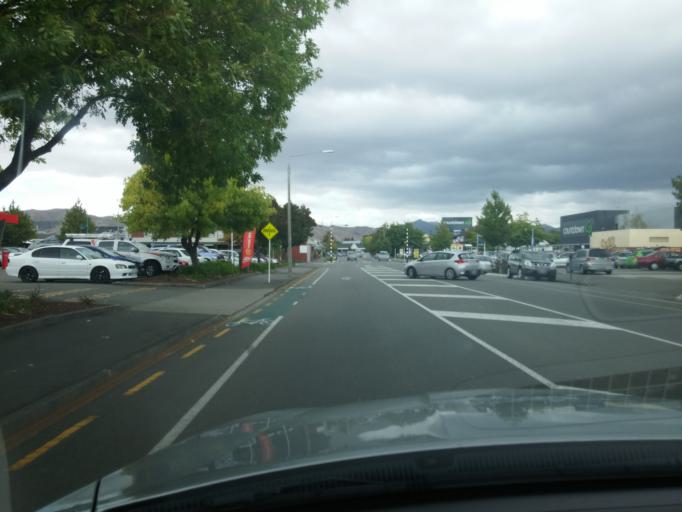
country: NZ
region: Marlborough
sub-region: Marlborough District
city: Blenheim
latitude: -41.5128
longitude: 173.9545
